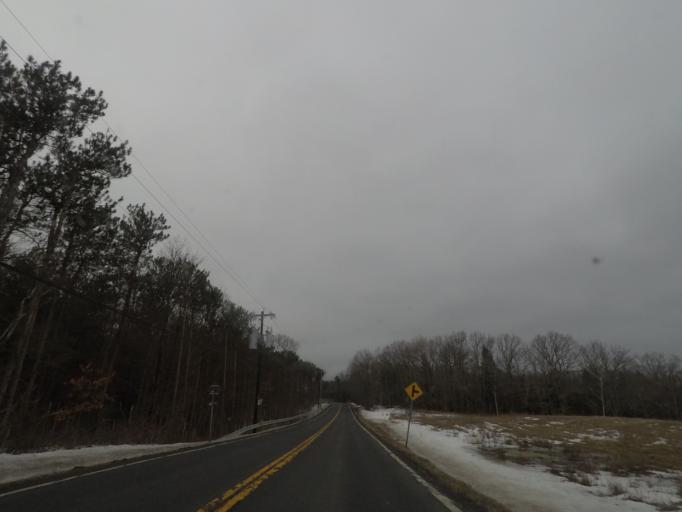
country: US
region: New York
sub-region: Albany County
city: Voorheesville
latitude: 42.6578
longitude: -73.9802
